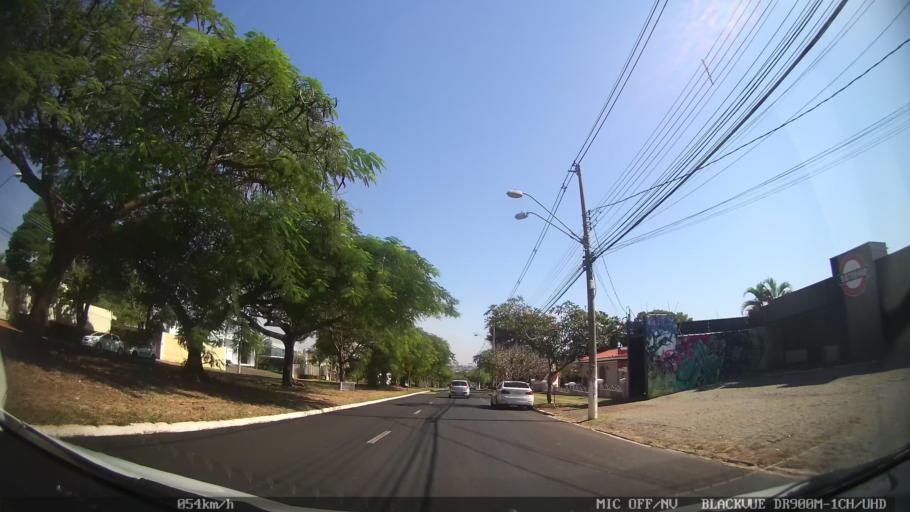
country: BR
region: Sao Paulo
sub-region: Ribeirao Preto
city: Ribeirao Preto
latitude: -21.2019
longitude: -47.7849
